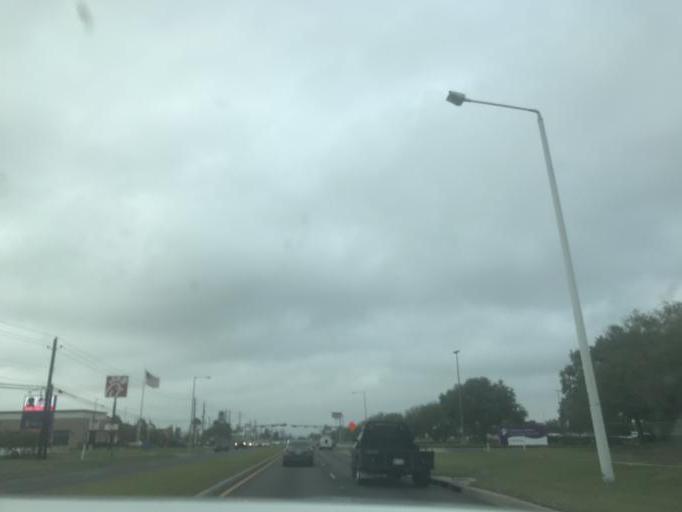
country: US
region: Texas
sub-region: Nueces County
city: Corpus Christi
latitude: 27.6823
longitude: -97.3774
